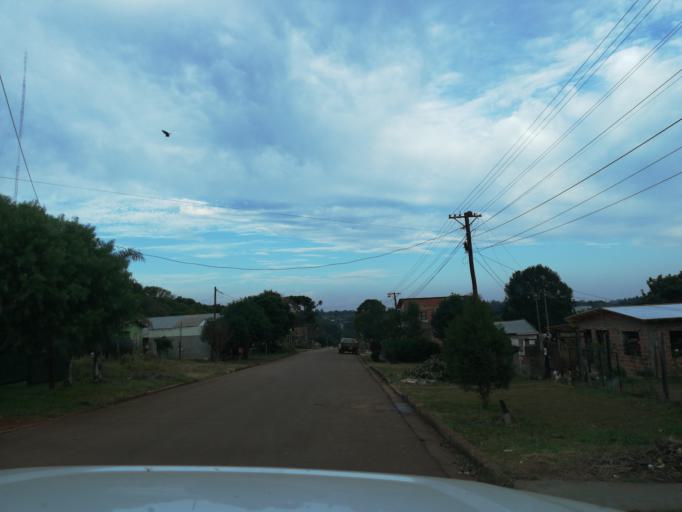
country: AR
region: Misiones
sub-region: Departamento de San Pedro
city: San Pedro
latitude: -26.6272
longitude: -54.1035
